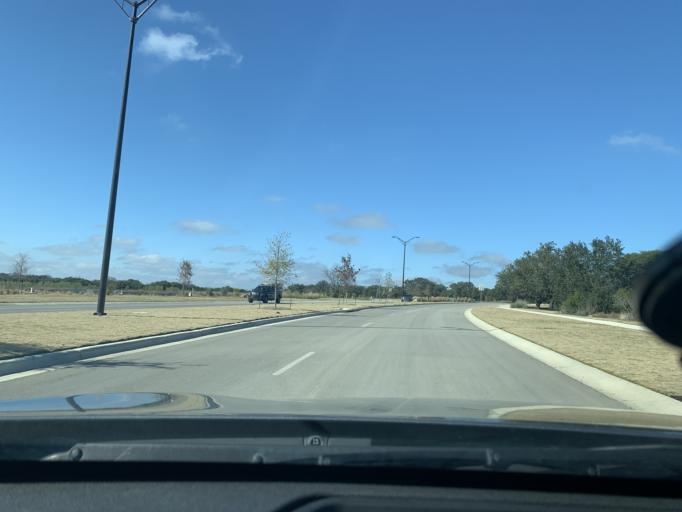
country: US
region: Texas
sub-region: Williamson County
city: Serenada
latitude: 30.7316
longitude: -97.7598
